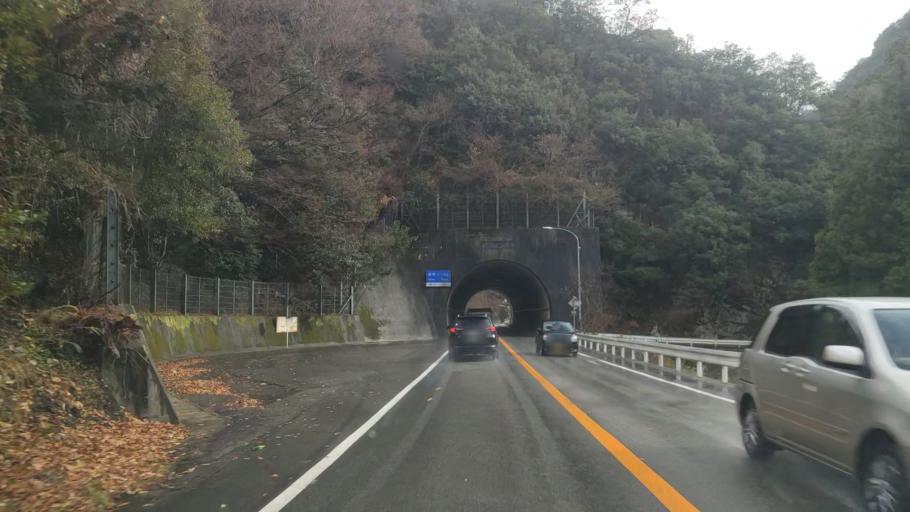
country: JP
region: Tokushima
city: Kamojimacho-jogejima
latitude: 34.1637
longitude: 134.3484
